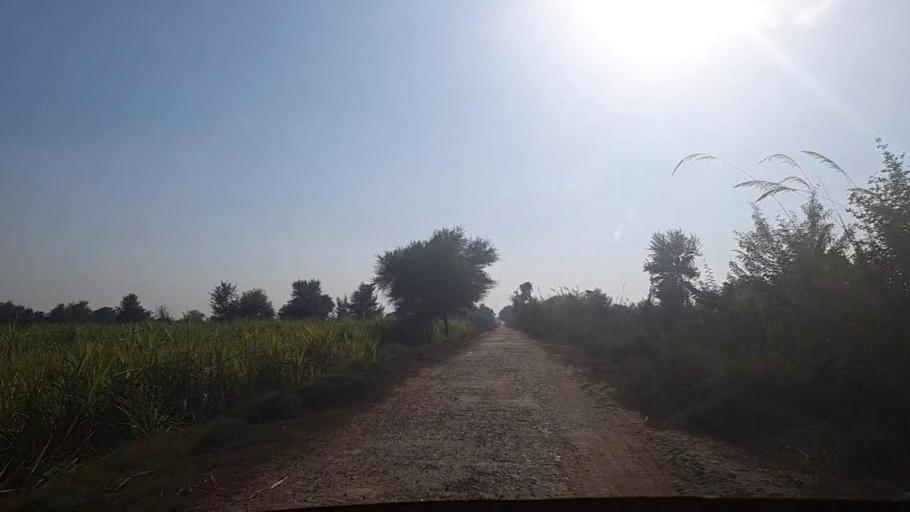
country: PK
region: Sindh
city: Gambat
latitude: 27.3687
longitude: 68.4623
